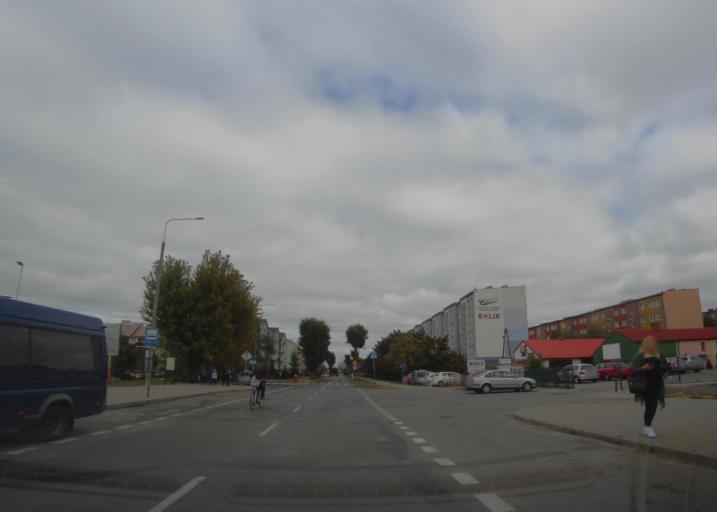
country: PL
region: Lublin Voivodeship
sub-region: Powiat wlodawski
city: Wlodawa
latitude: 51.5478
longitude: 23.5450
